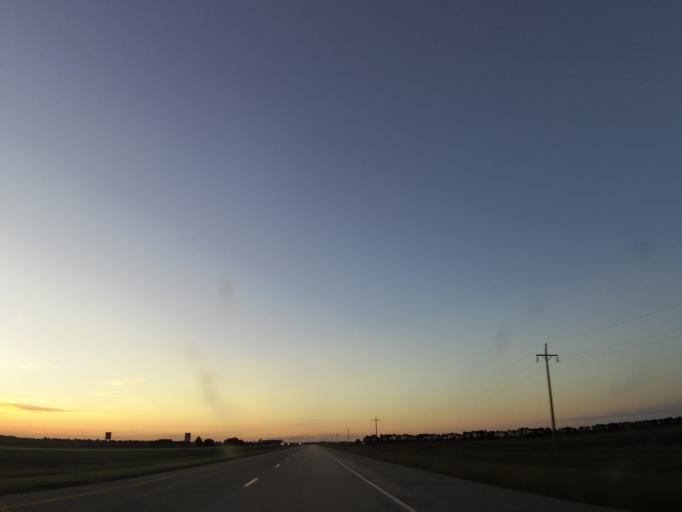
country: US
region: North Dakota
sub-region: Walsh County
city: Grafton
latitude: 48.3591
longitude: -97.1893
